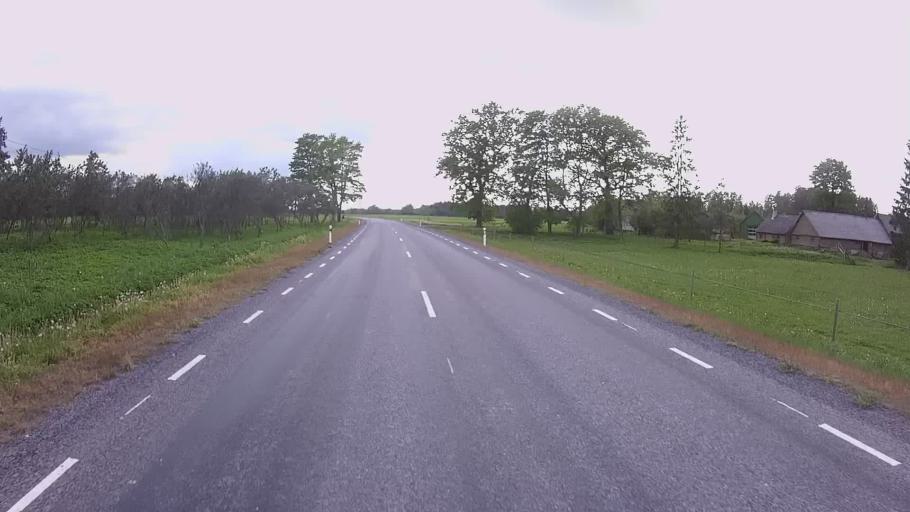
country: EE
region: Jogevamaa
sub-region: Mustvee linn
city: Mustvee
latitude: 59.0086
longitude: 26.9222
